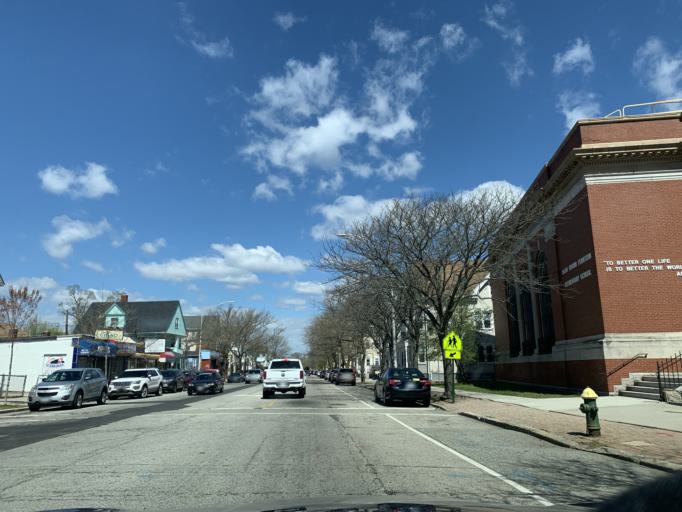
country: US
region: Rhode Island
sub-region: Providence County
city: Cranston
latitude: 41.7879
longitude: -71.4032
